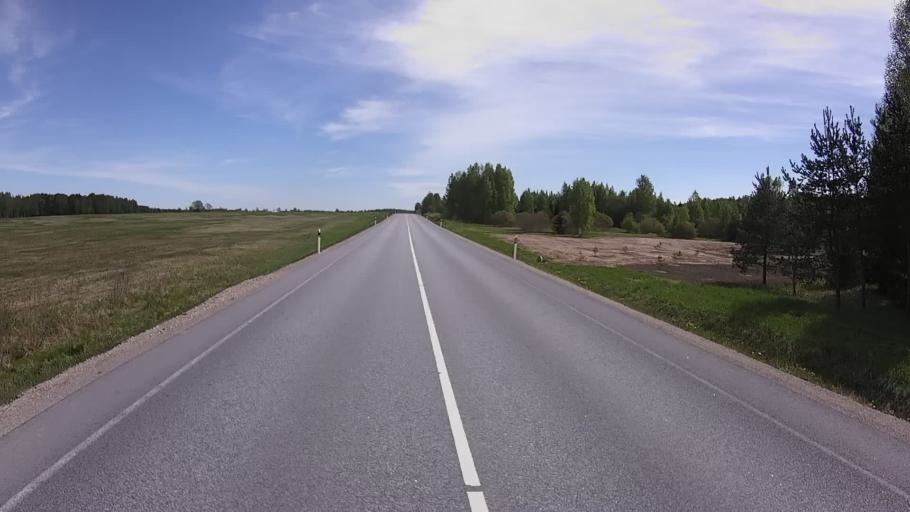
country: EE
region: Valgamaa
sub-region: Valga linn
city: Valga
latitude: 57.7244
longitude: 26.1868
